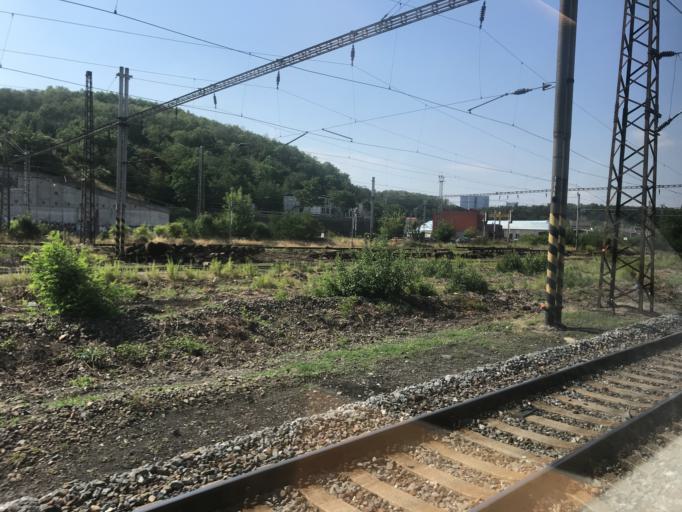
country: CZ
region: Praha
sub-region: Praha 8
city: Karlin
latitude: 50.0644
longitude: 14.4624
